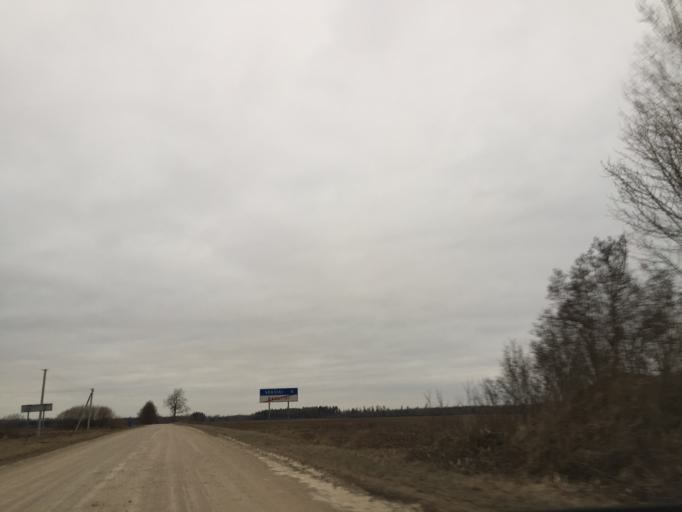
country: LT
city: Zagare
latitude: 56.2729
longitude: 23.2625
